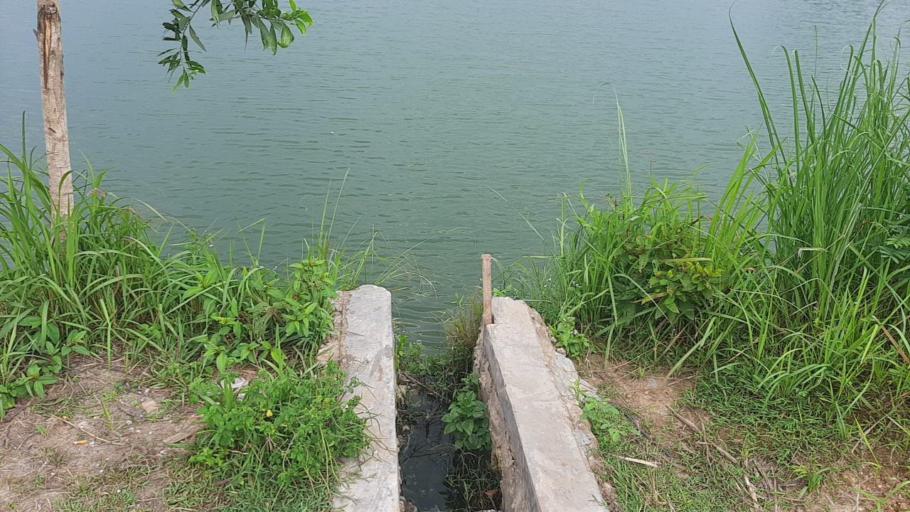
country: ID
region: West Java
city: Cileungsir
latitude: -6.4418
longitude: 107.0244
